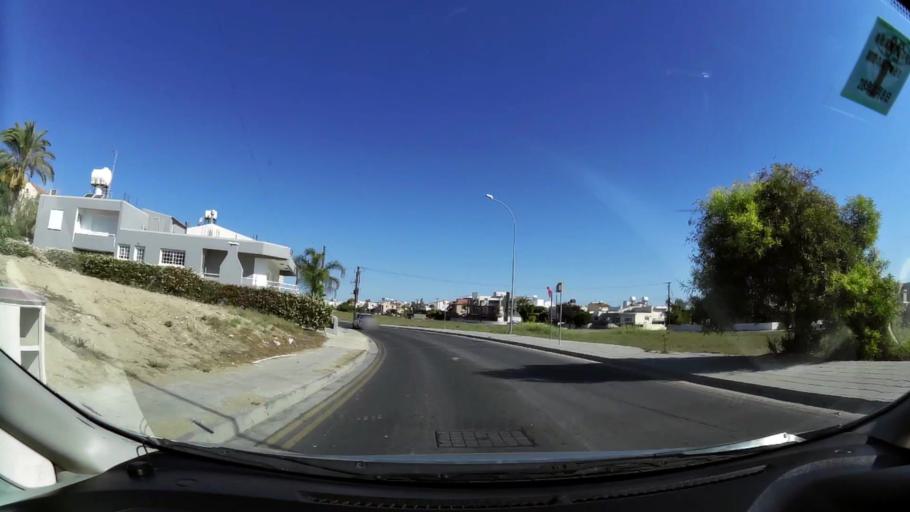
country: CY
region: Larnaka
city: Livadia
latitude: 34.9400
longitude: 33.6285
